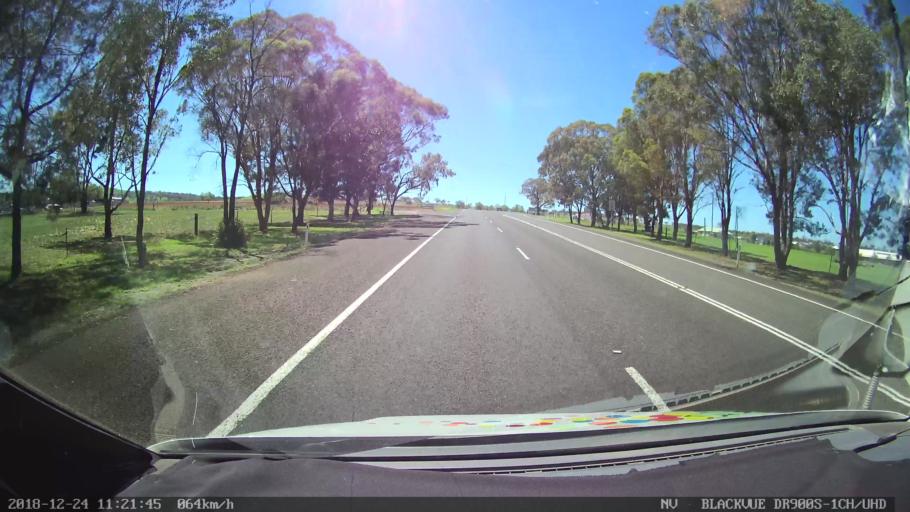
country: AU
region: New South Wales
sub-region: Upper Hunter Shire
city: Merriwa
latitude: -32.1448
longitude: 150.3730
